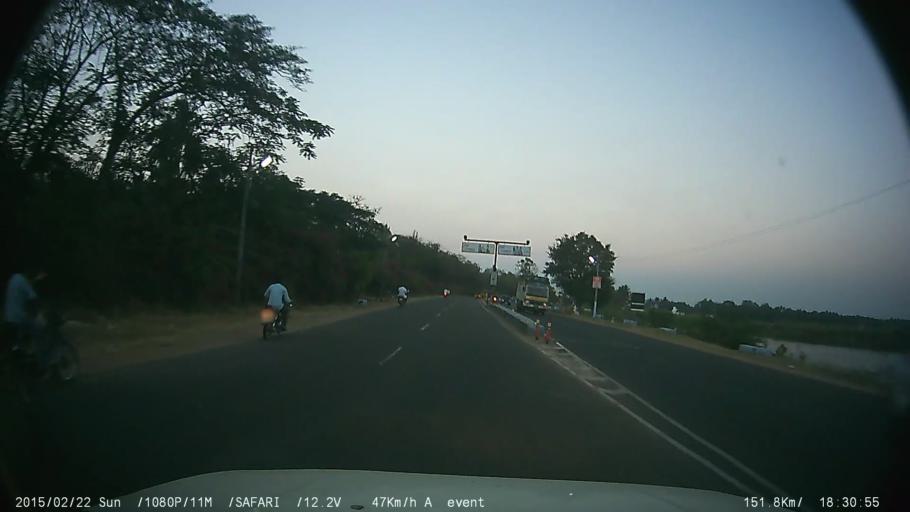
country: IN
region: Tamil Nadu
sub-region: Theni
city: Teni
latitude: 9.9910
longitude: 77.4592
